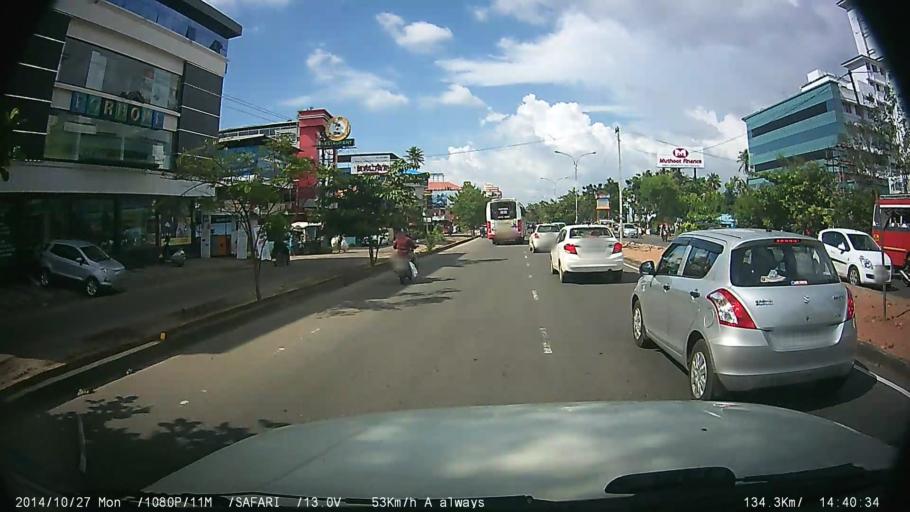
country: IN
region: Kerala
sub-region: Ernakulam
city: Elur
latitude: 9.9983
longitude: 76.3142
